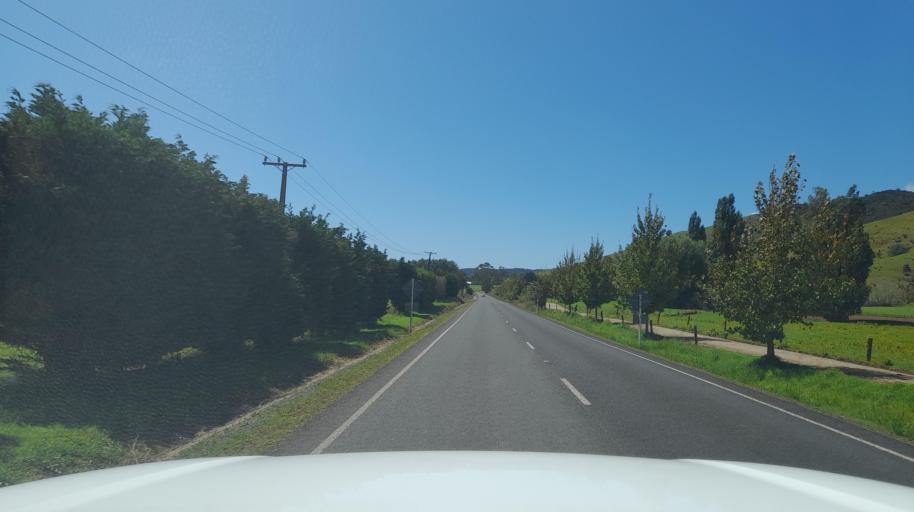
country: NZ
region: Northland
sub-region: Far North District
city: Taipa
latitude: -35.0665
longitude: 173.5022
